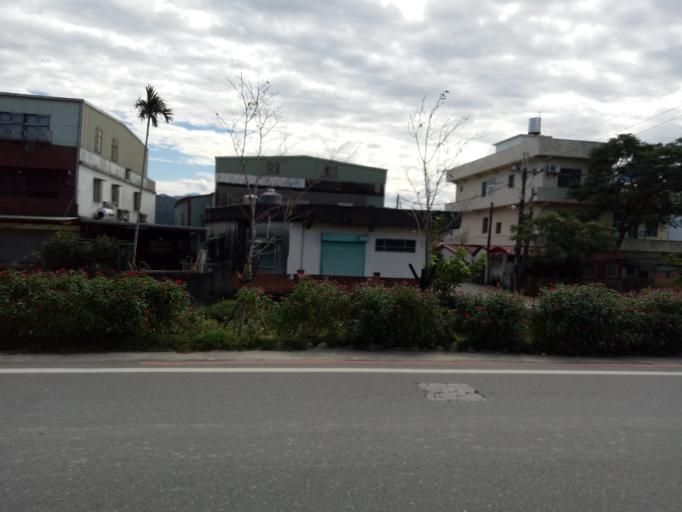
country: TW
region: Taiwan
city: Daxi
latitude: 24.9300
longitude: 121.3181
